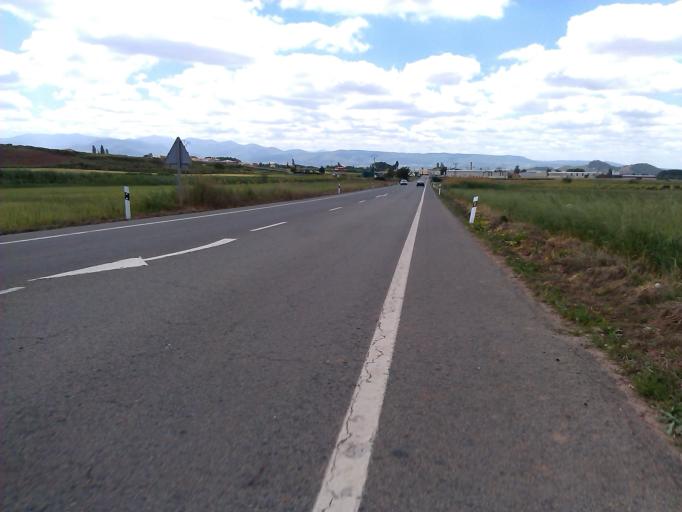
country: ES
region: La Rioja
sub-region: Provincia de La Rioja
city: Aleson
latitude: 42.4116
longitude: -2.6781
